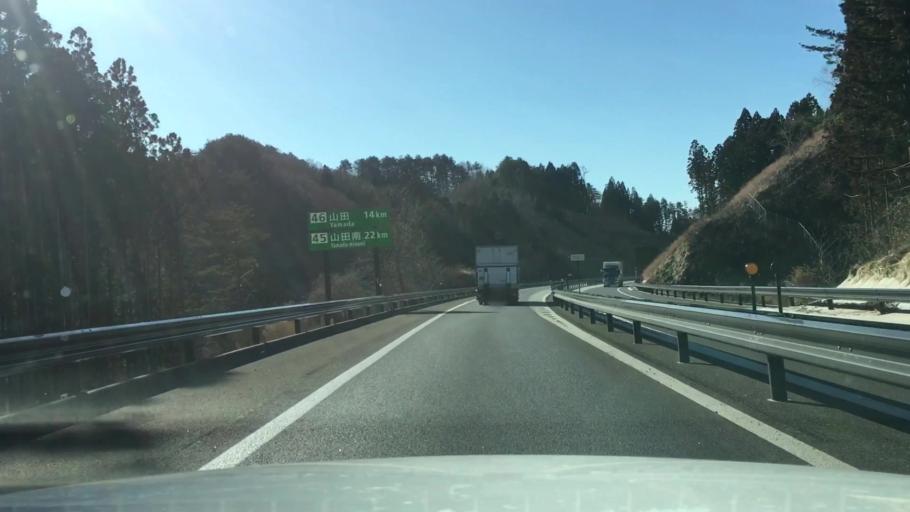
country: JP
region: Iwate
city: Miyako
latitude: 39.5910
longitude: 141.9404
